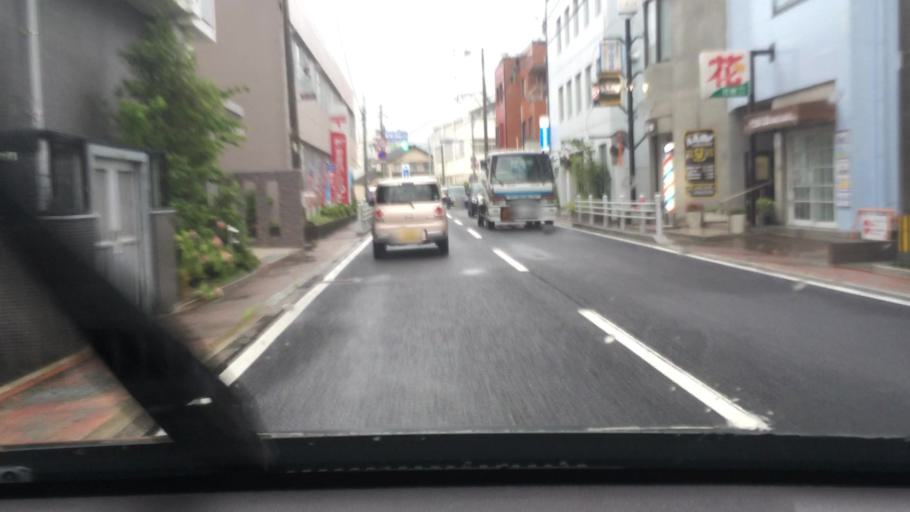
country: JP
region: Nagasaki
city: Sasebo
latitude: 33.1350
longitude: 129.7984
